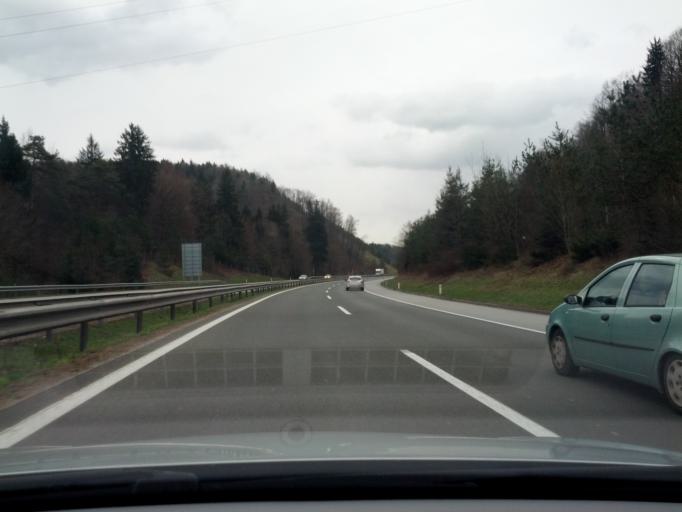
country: SI
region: Skofljica
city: Skofljica
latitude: 46.0019
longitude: 14.5811
